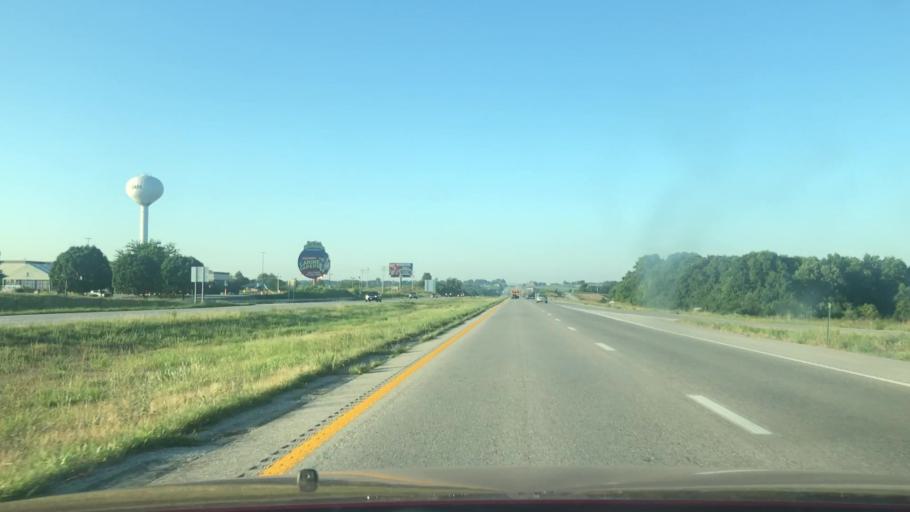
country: US
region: Missouri
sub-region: Christian County
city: Ozark
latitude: 37.0035
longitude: -93.2299
